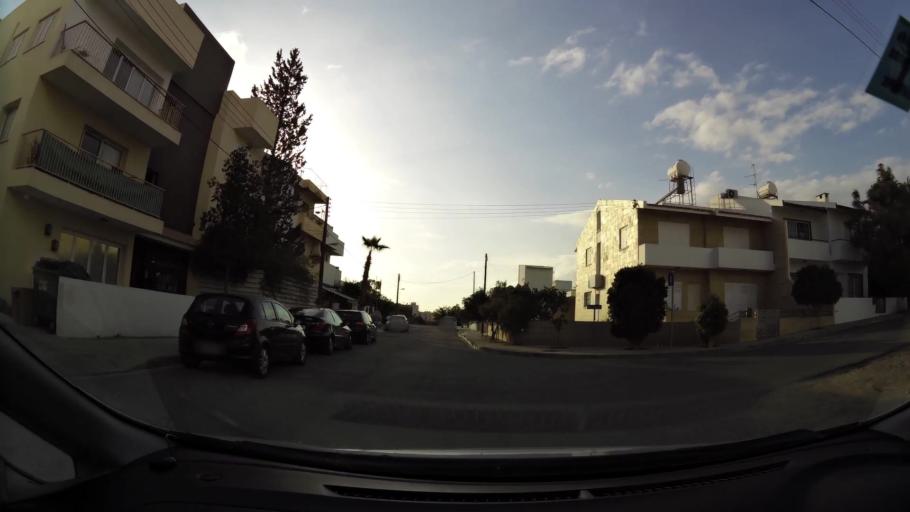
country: CY
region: Lefkosia
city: Nicosia
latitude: 35.1633
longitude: 33.3912
